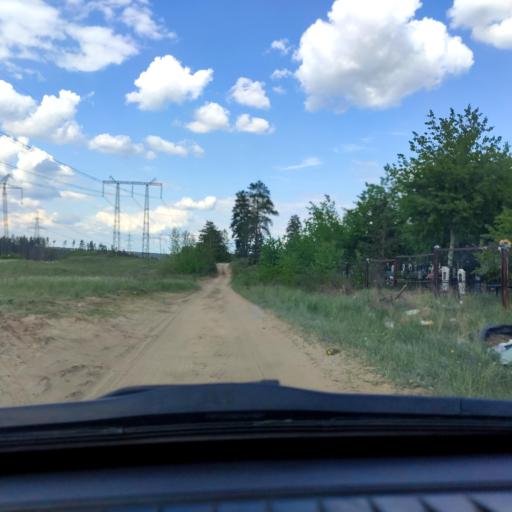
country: RU
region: Samara
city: Zhigulevsk
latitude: 53.5337
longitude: 49.5466
